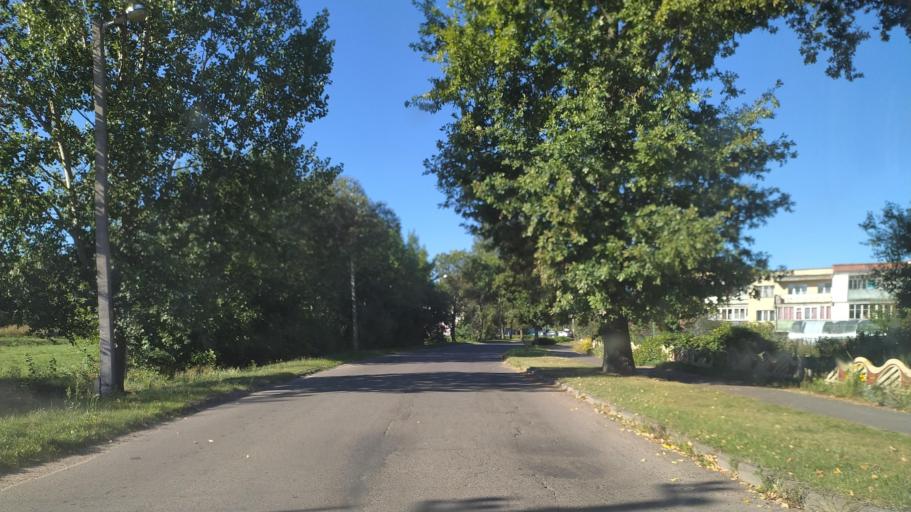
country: BY
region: Brest
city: Pruzhany
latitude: 52.4884
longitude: 24.7104
